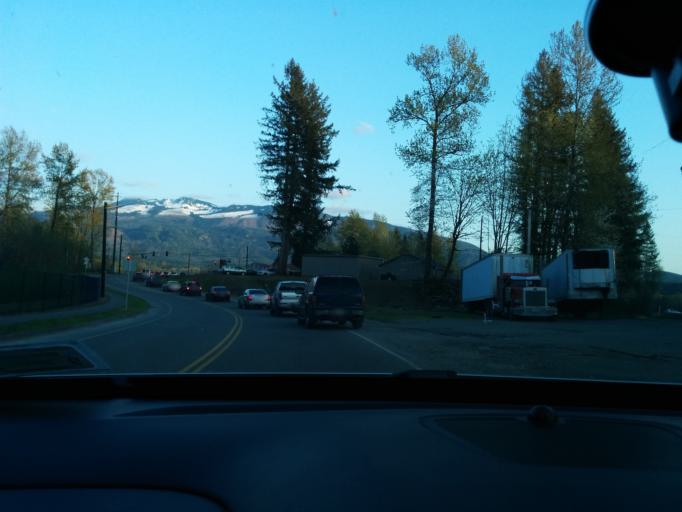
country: US
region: Washington
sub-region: Snohomish County
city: Sultan
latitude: 47.8664
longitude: -121.7990
